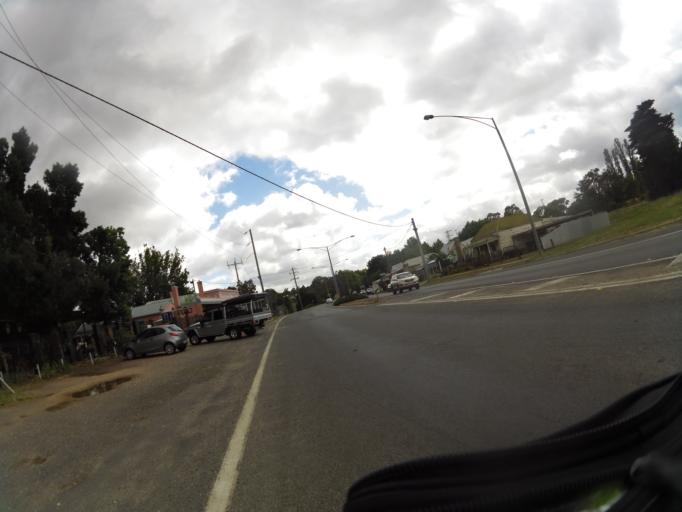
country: AU
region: Victoria
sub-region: Mount Alexander
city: Castlemaine
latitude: -37.0733
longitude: 144.2063
